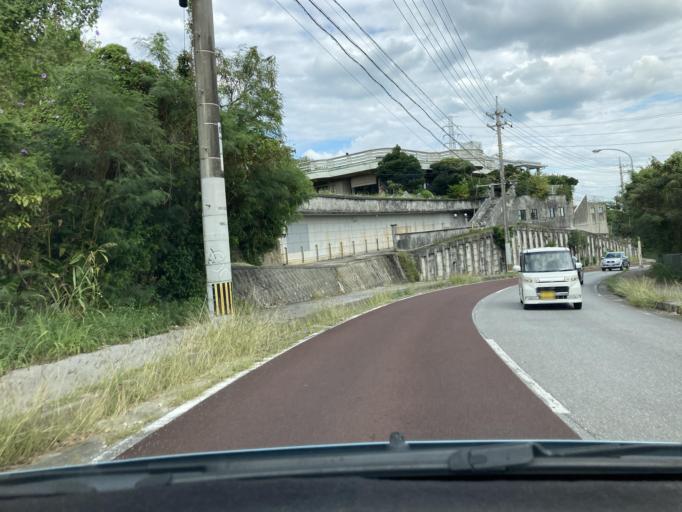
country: JP
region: Okinawa
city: Gushikawa
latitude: 26.3512
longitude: 127.8396
